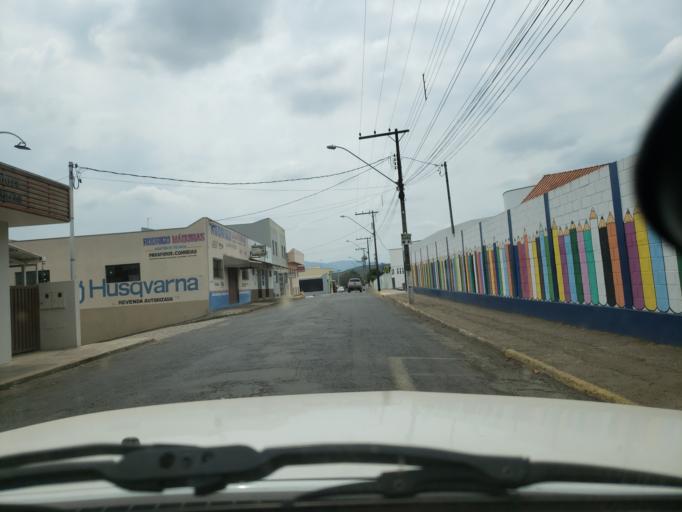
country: BR
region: Minas Gerais
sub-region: Jacutinga
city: Jacutinga
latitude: -22.2805
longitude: -46.6078
